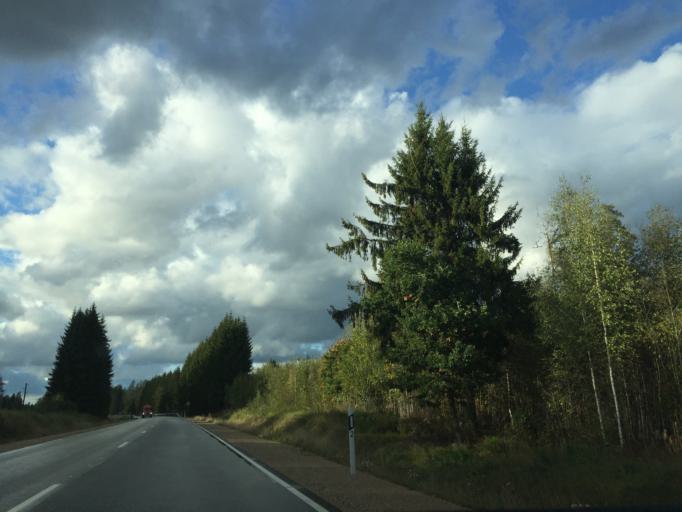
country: LV
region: Ligatne
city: Ligatne
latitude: 57.1512
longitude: 25.0723
